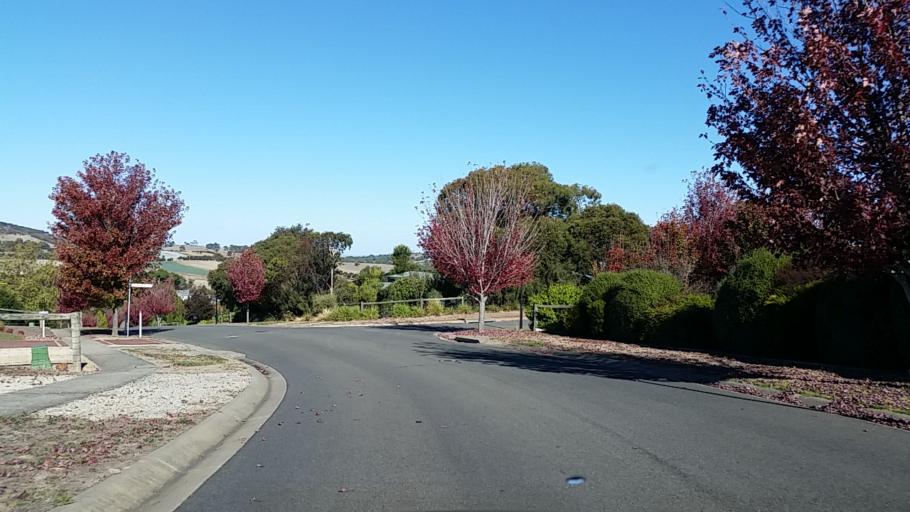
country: AU
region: South Australia
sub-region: Mount Barker
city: Mount Barker
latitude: -35.0622
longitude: 138.8858
